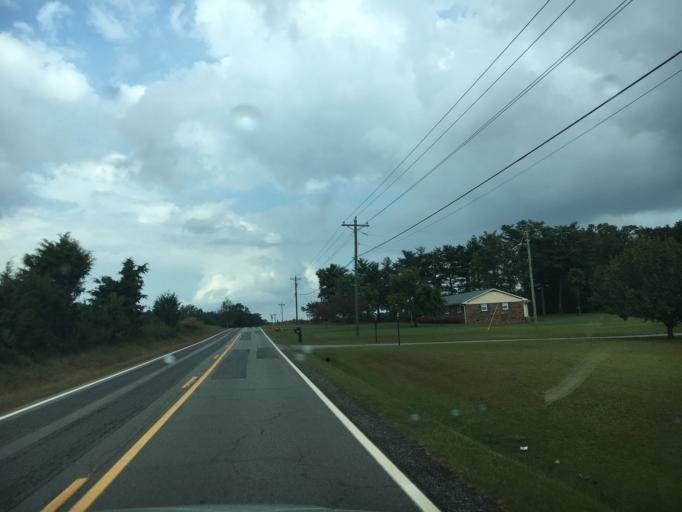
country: US
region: Georgia
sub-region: Hart County
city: Reed Creek
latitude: 34.4308
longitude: -82.9380
